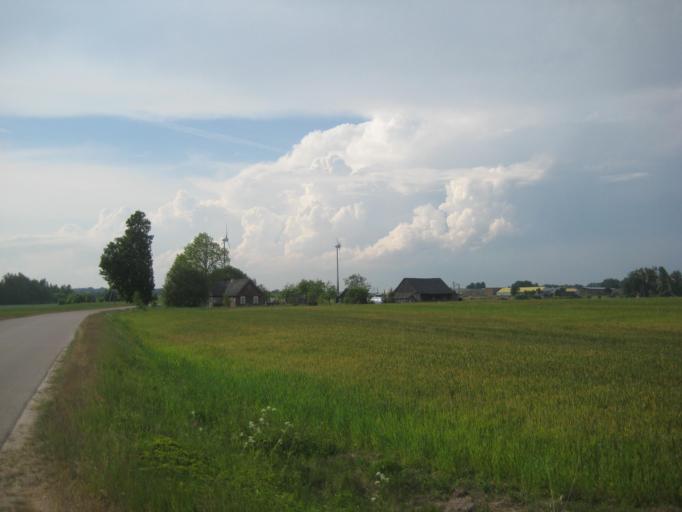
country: LT
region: Panevezys
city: Rokiskis
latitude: 55.8524
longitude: 25.7443
